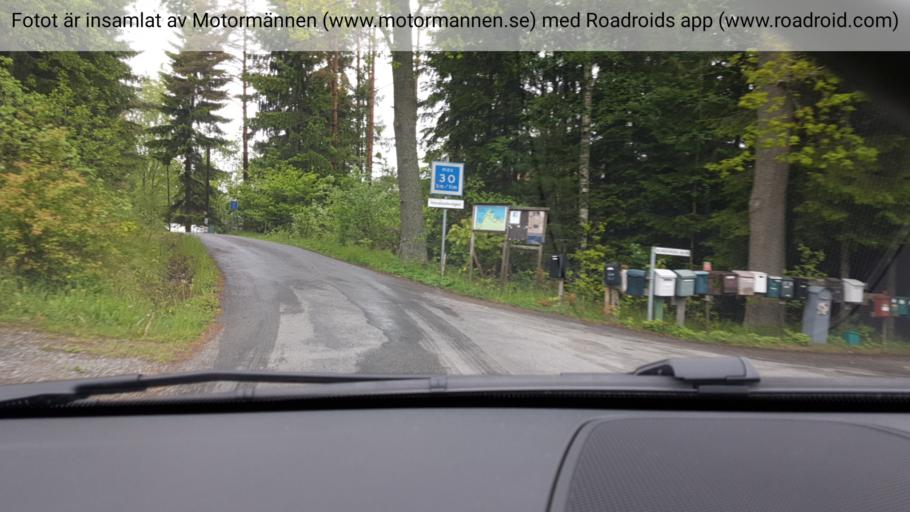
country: SE
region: Stockholm
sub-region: Haninge Kommun
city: Jordbro
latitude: 59.0169
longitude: 18.1154
